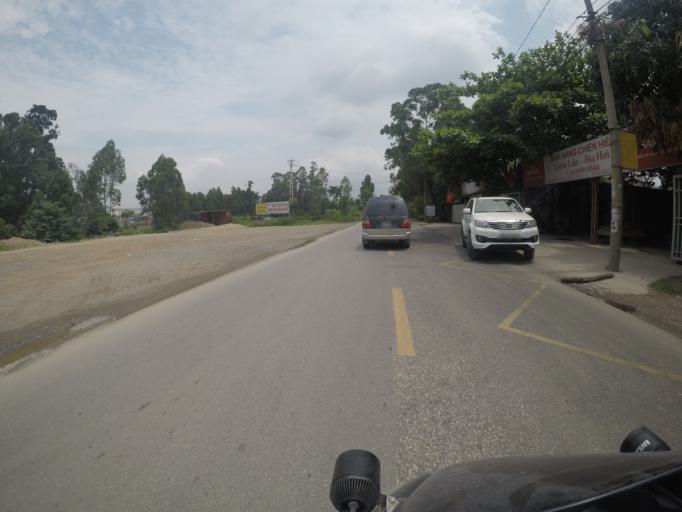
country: VN
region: Ha Noi
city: Soc Son
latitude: 21.2167
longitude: 105.8489
